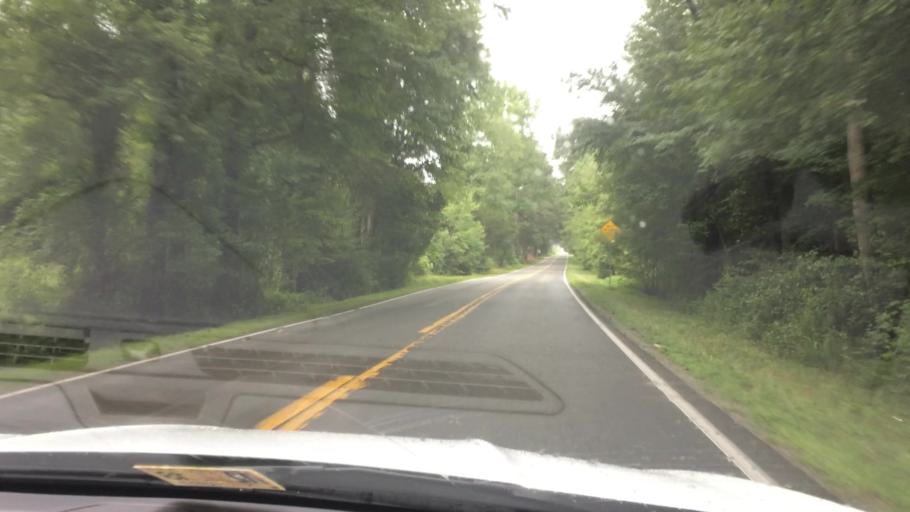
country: US
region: Virginia
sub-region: Charles City County
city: Charles City
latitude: 37.4240
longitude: -77.0399
